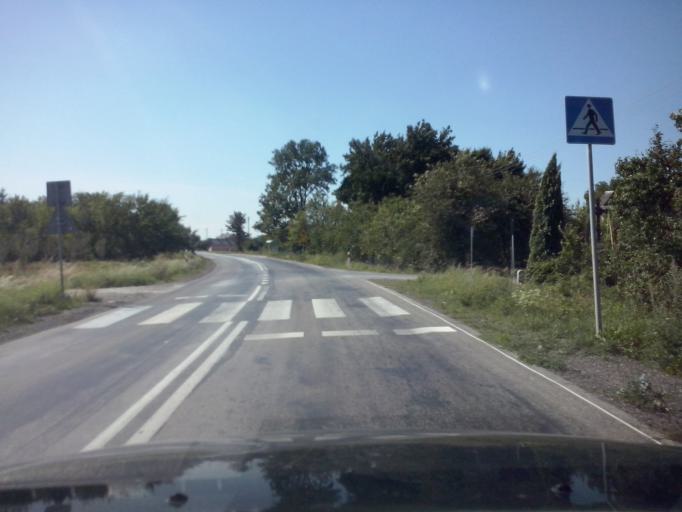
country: PL
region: Swietokrzyskie
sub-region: Powiat staszowski
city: Szydlow
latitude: 50.6132
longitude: 21.0096
